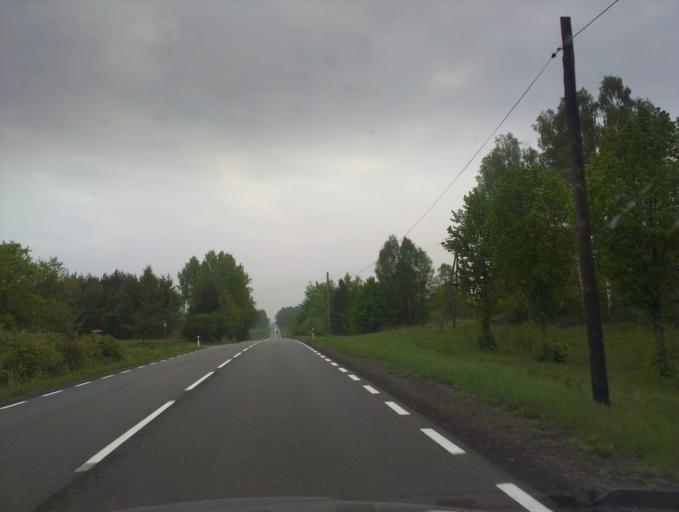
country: PL
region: West Pomeranian Voivodeship
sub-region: Powiat koszalinski
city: Bobolice
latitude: 53.8801
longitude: 16.6138
